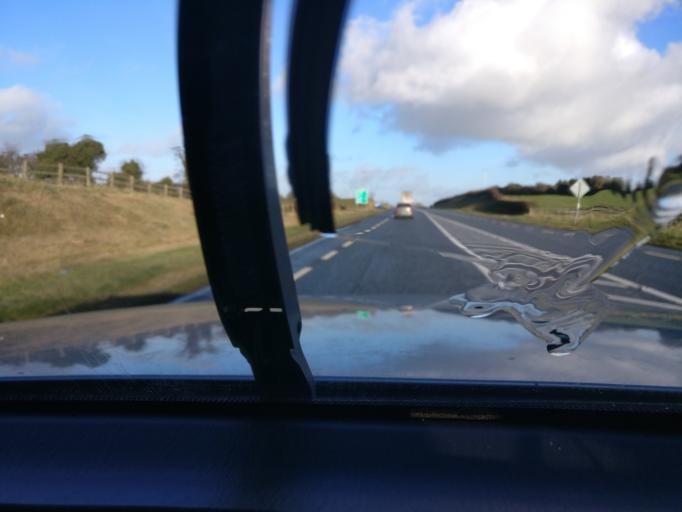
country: IE
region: Leinster
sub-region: An Iarmhi
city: Rathwire
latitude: 53.5967
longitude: -7.1117
